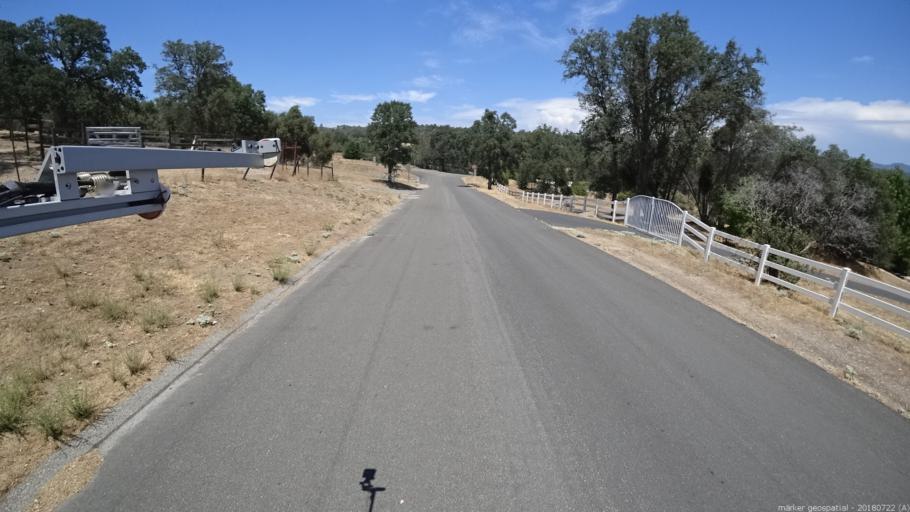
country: US
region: California
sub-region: Madera County
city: Yosemite Lakes
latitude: 37.2147
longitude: -119.7312
